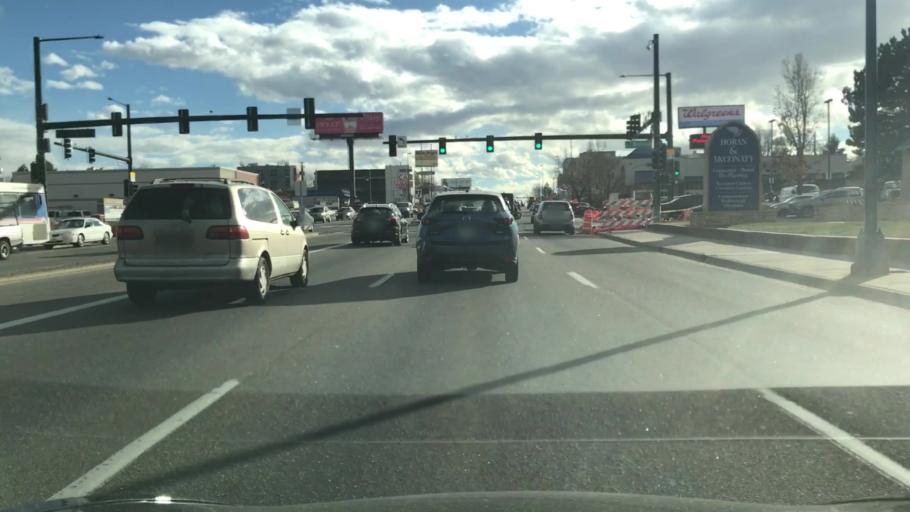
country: US
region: Colorado
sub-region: Arapahoe County
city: Glendale
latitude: 39.6971
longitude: -104.9408
